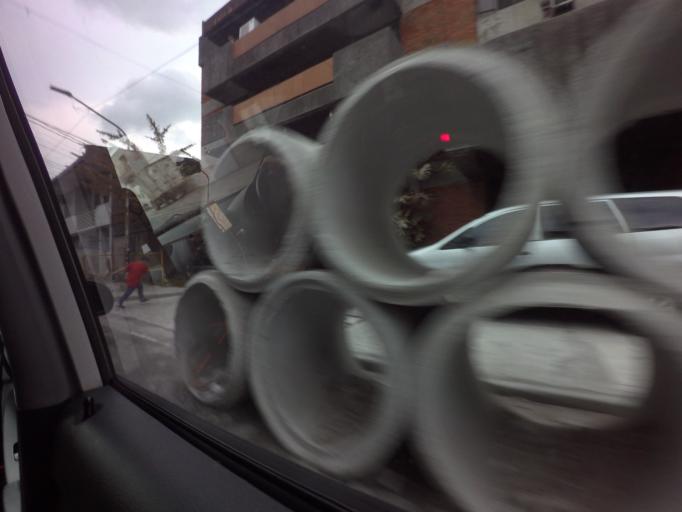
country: PH
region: Calabarzon
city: Del Monte
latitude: 14.6206
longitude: 121.0072
